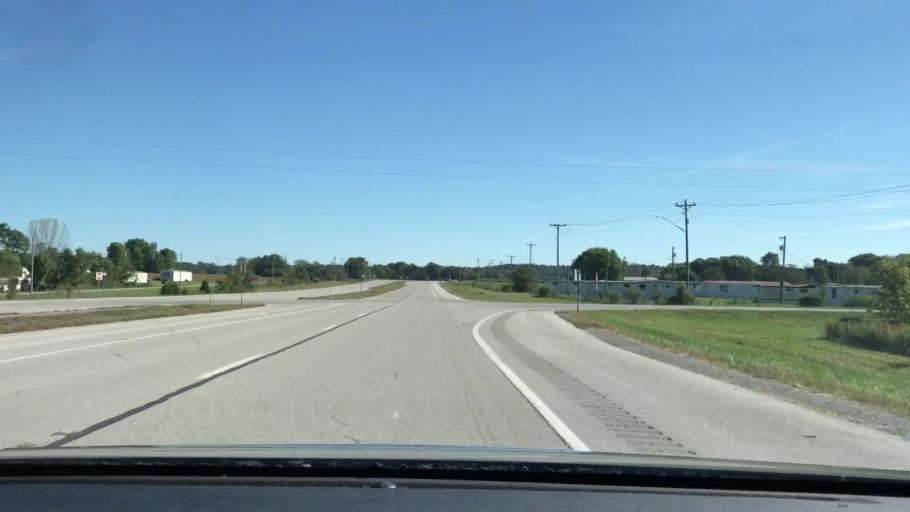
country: US
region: Kentucky
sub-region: Todd County
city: Elkton
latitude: 36.8227
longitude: -87.1658
